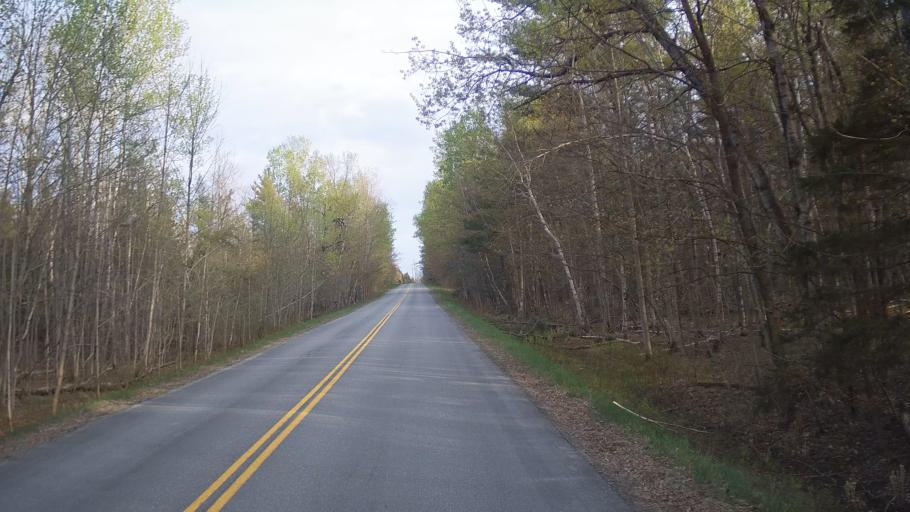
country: US
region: Vermont
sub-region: Orleans County
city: Newport
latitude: 44.9392
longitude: -72.4370
